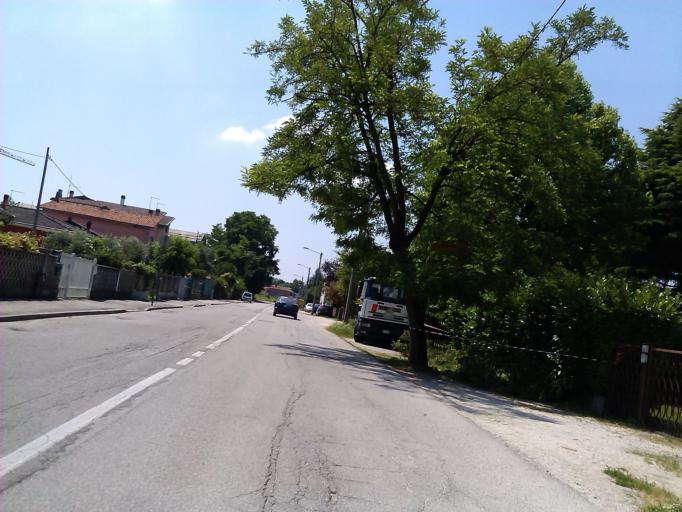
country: IT
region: Veneto
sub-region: Provincia di Venezia
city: Fornase
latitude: 45.4567
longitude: 12.1804
